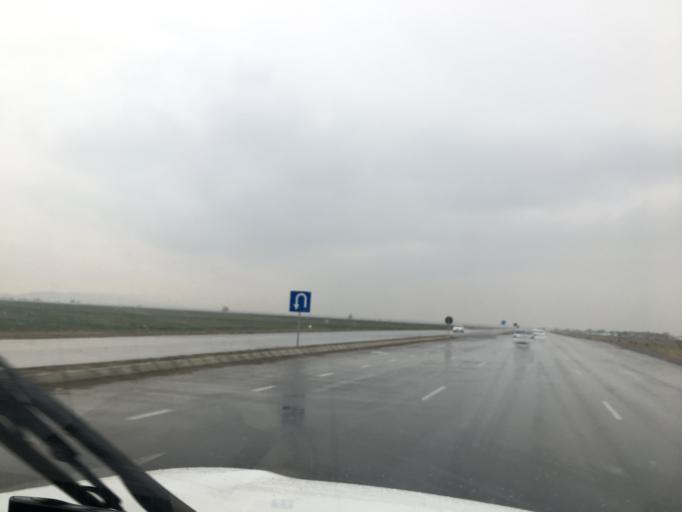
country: TM
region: Ahal
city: Annau
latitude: 37.8203
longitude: 58.7656
